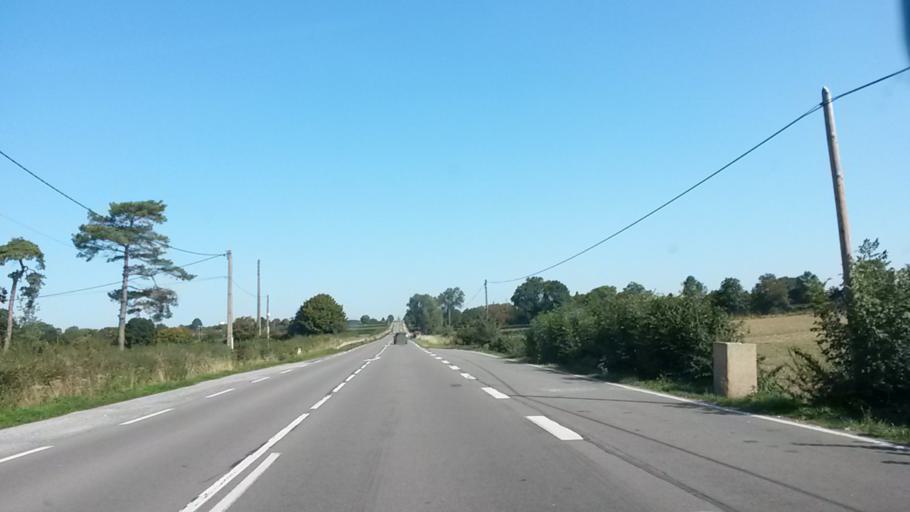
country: FR
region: Nord-Pas-de-Calais
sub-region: Departement du Nord
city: Avesnes-sur-Helpe
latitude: 50.0960
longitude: 3.9306
